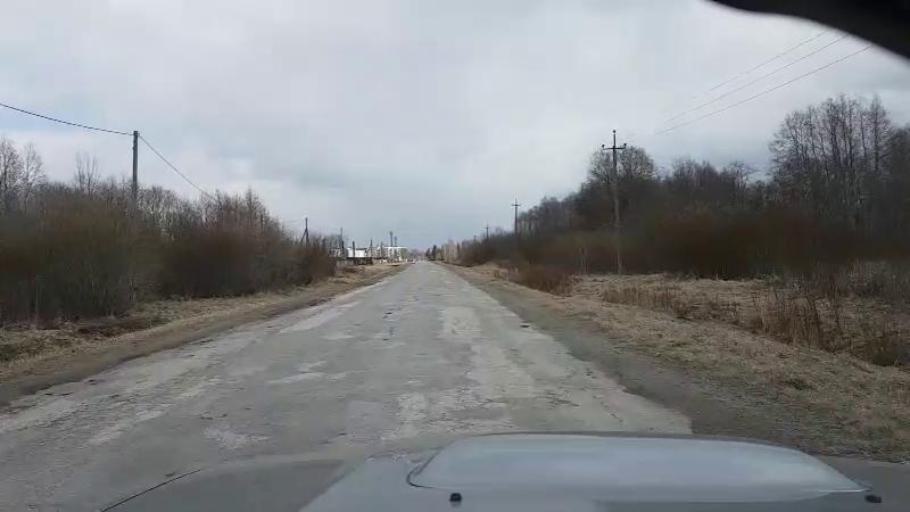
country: EE
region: Jaervamaa
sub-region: Paide linn
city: Paide
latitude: 58.8768
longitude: 25.5563
